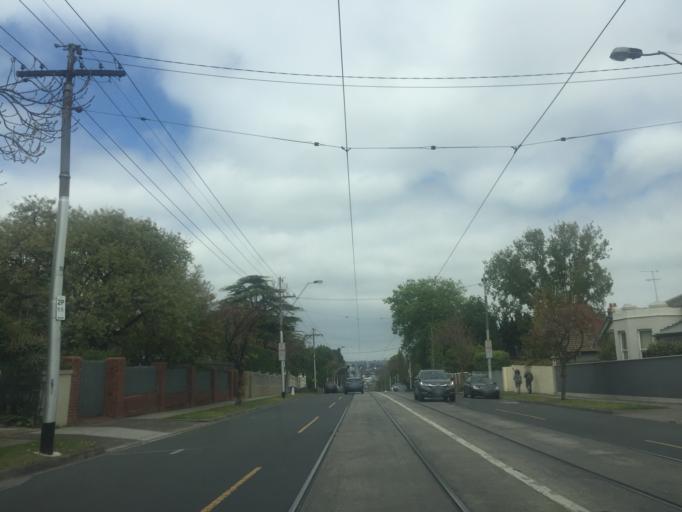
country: AU
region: Victoria
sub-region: Boroondara
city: Kew
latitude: -37.8107
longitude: 145.0376
